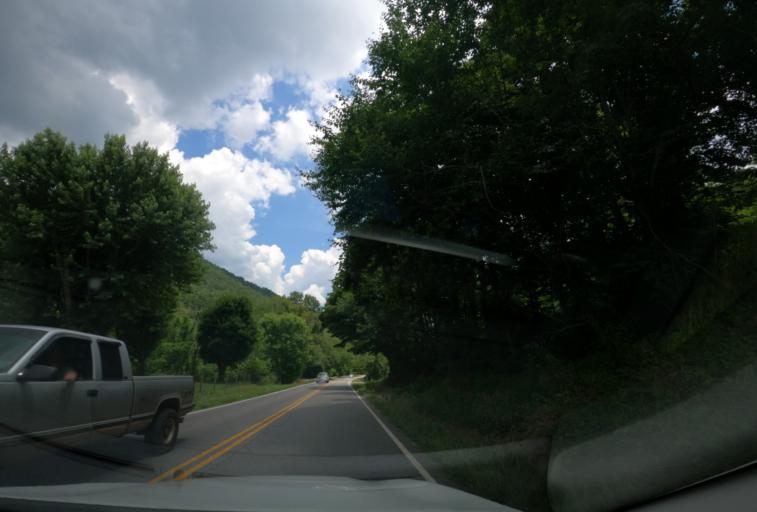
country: US
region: North Carolina
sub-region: Haywood County
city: Waynesville
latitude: 35.4734
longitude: -82.9325
